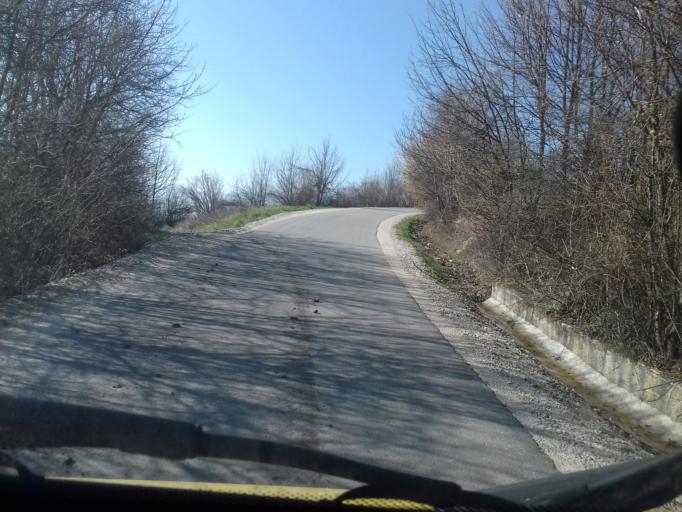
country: BA
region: Federation of Bosnia and Herzegovina
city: Travnik
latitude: 44.2461
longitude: 17.7333
